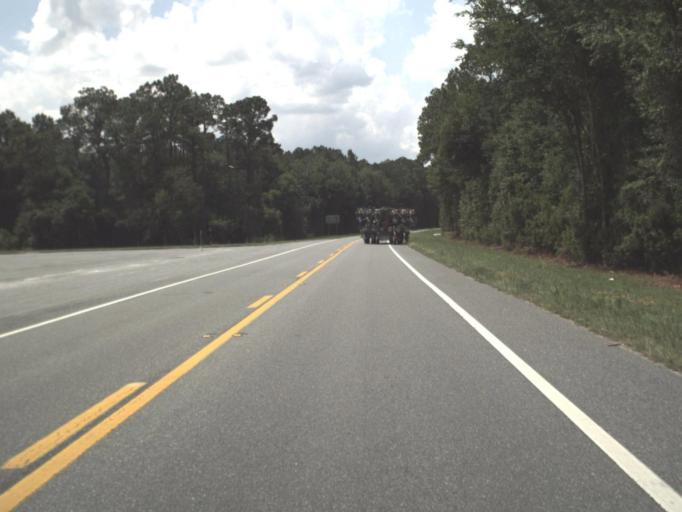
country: US
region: Georgia
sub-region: Echols County
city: Statenville
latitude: 30.6175
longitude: -83.1145
